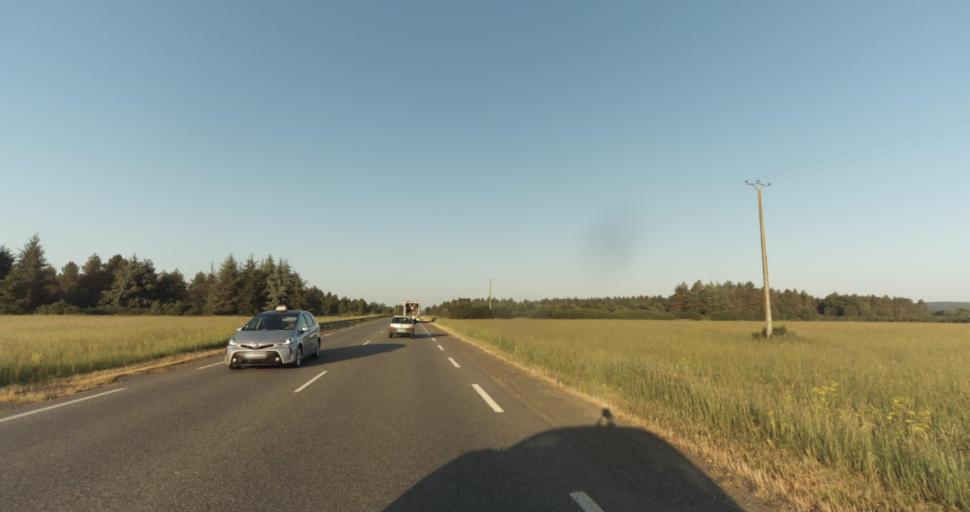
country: FR
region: Midi-Pyrenees
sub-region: Departement de la Haute-Garonne
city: Fontenilles
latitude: 43.5739
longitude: 1.2068
